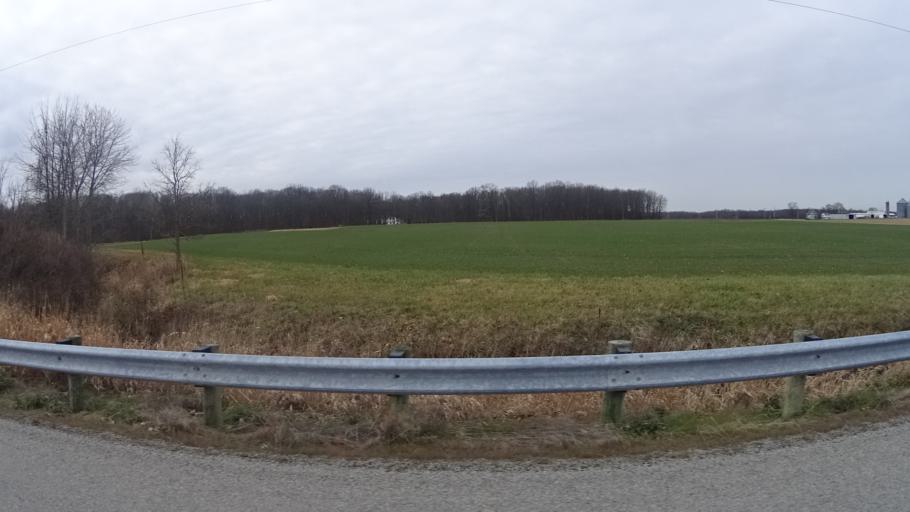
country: US
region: Ohio
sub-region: Lorain County
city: Wellington
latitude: 41.1979
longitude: -82.1927
